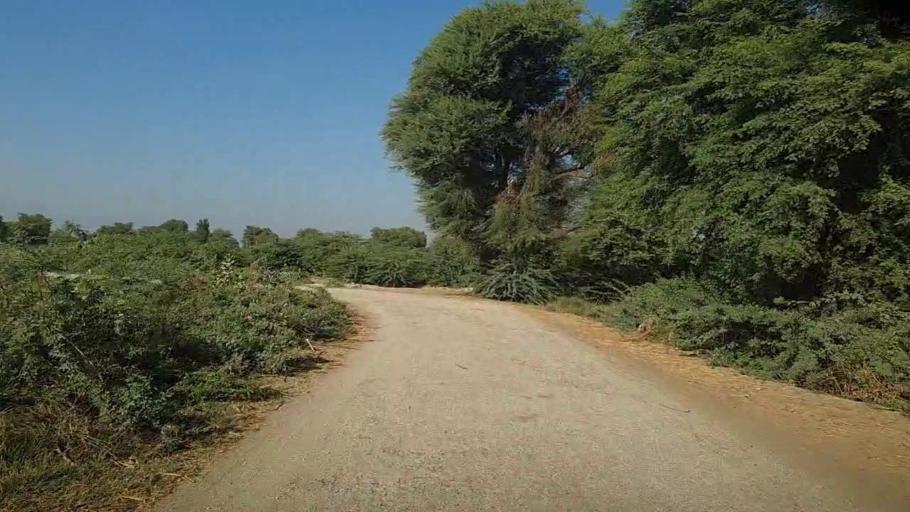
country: PK
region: Sindh
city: Darya Khan Marri
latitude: 26.6892
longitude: 68.3517
